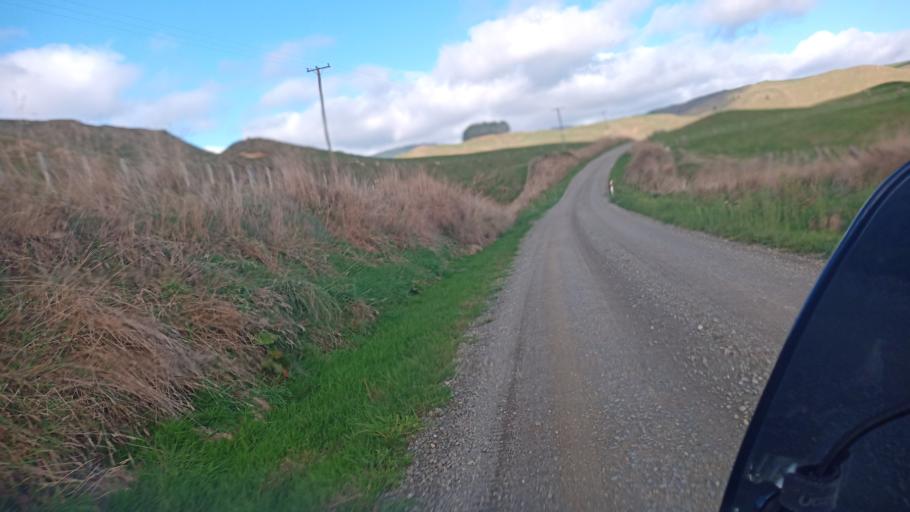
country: NZ
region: Bay of Plenty
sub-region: Opotiki District
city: Opotiki
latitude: -38.4565
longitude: 177.3926
